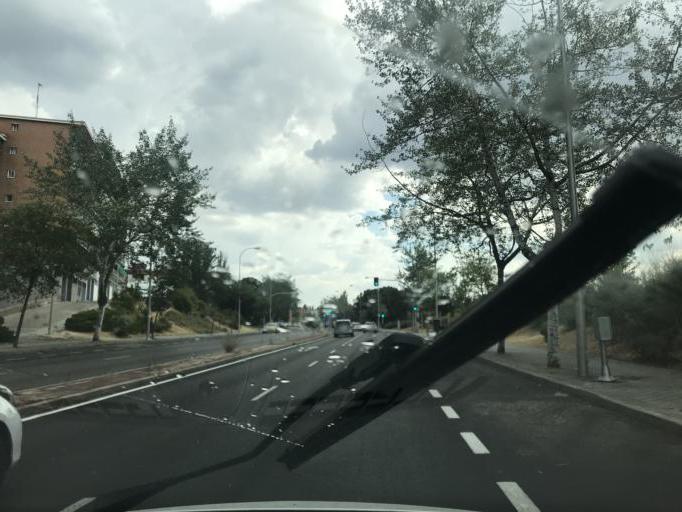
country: ES
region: Madrid
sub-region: Provincia de Madrid
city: Pinar de Chamartin
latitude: 40.4758
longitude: -3.6551
